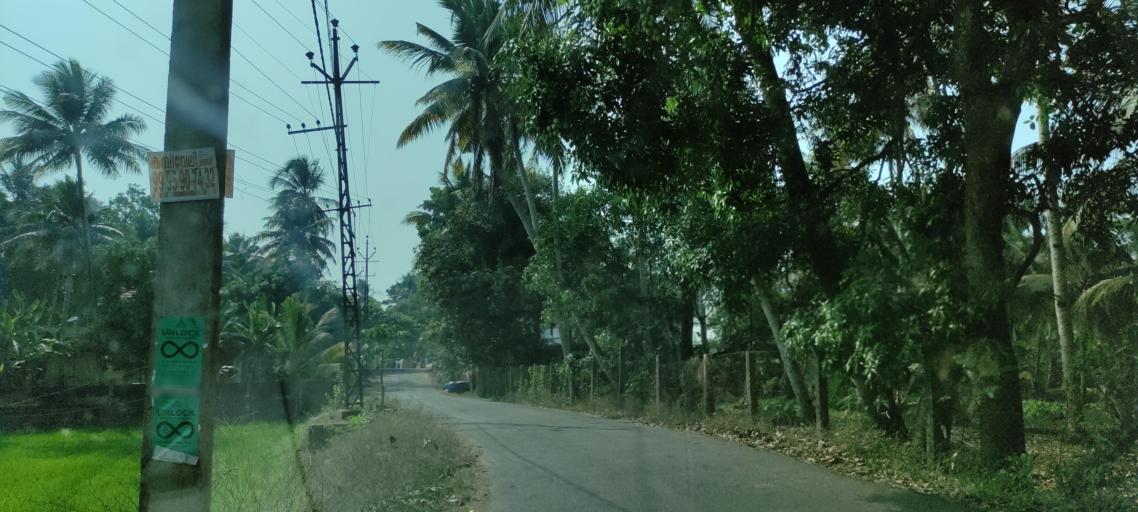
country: IN
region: Kerala
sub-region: Pattanamtitta
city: Tiruvalla
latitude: 9.3608
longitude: 76.5055
